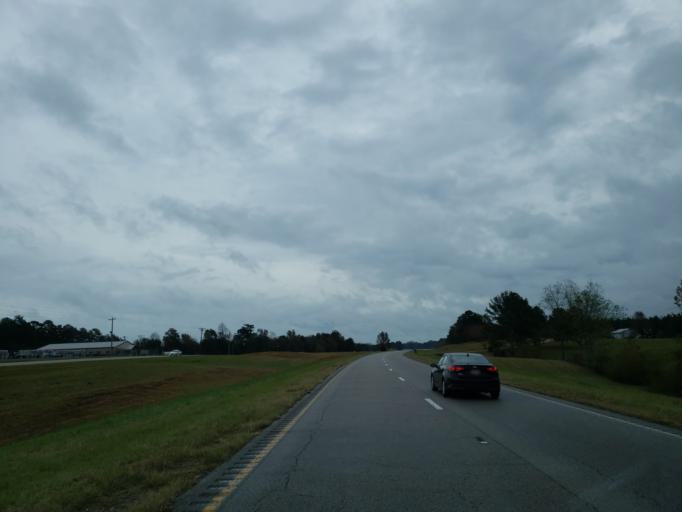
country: US
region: Mississippi
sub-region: Jones County
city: Sharon
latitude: 31.7028
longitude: -88.9106
